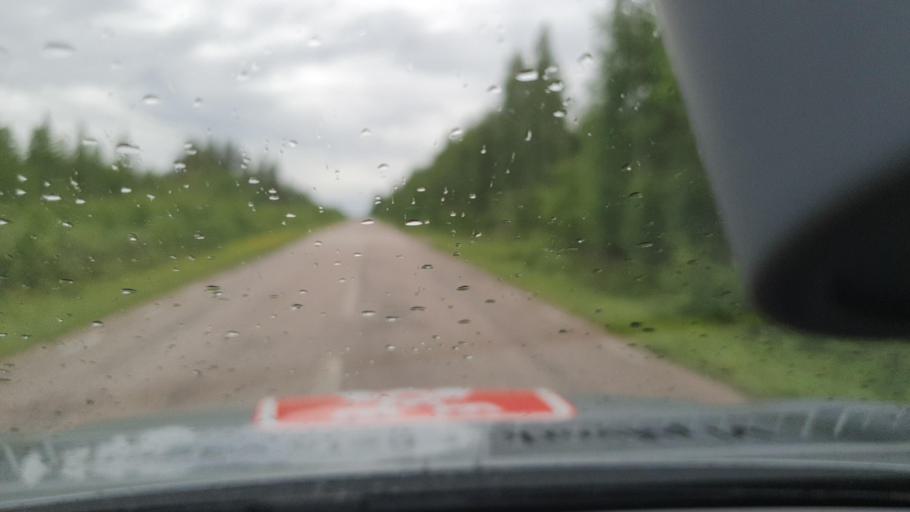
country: SE
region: Norrbotten
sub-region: Overkalix Kommun
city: OEverkalix
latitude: 66.4110
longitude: 22.7863
